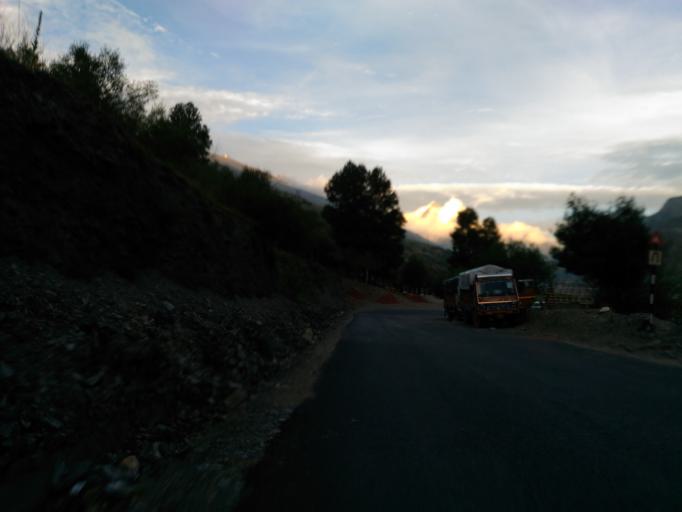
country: IN
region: Himachal Pradesh
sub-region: Lahul and Spiti
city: Kyelang
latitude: 32.5105
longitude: 77.0066
